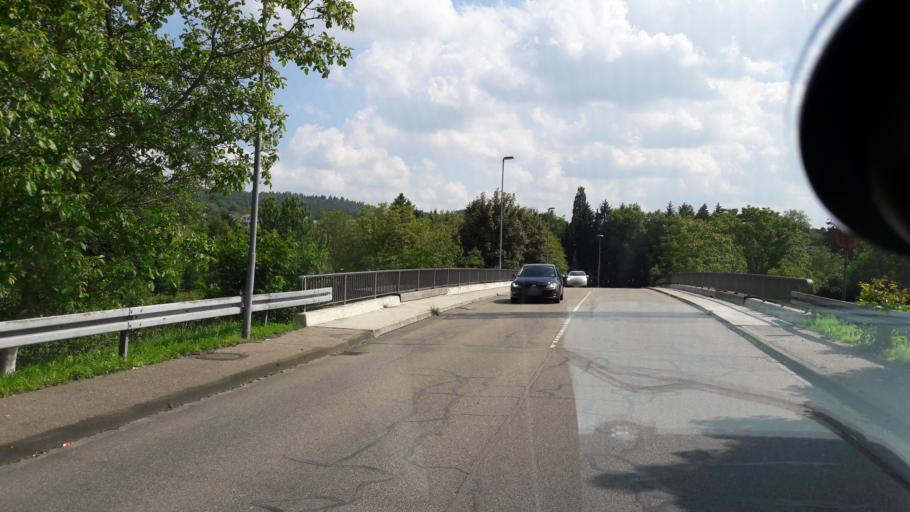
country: DE
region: Baden-Wuerttemberg
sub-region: Karlsruhe Region
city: Weingarten
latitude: 49.0066
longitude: 8.5177
